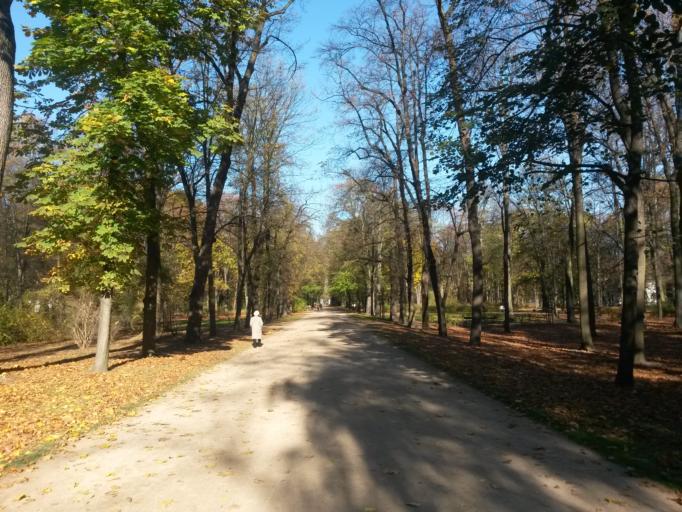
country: PL
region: Masovian Voivodeship
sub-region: Warszawa
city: Mokotow
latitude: 52.2135
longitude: 21.0329
